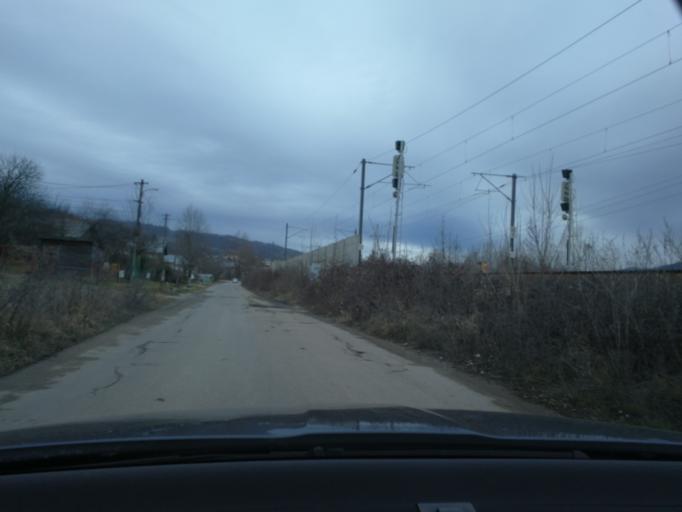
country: RO
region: Prahova
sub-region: Comuna Poiana Campina
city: Poiana Campina
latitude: 45.1406
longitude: 25.6979
